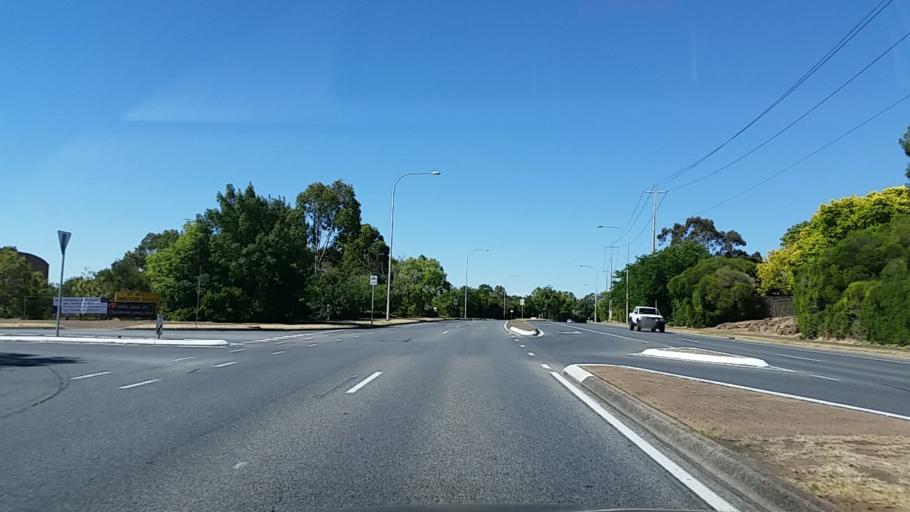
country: AU
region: South Australia
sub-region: Tea Tree Gully
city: Modbury
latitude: -34.7977
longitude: 138.6865
